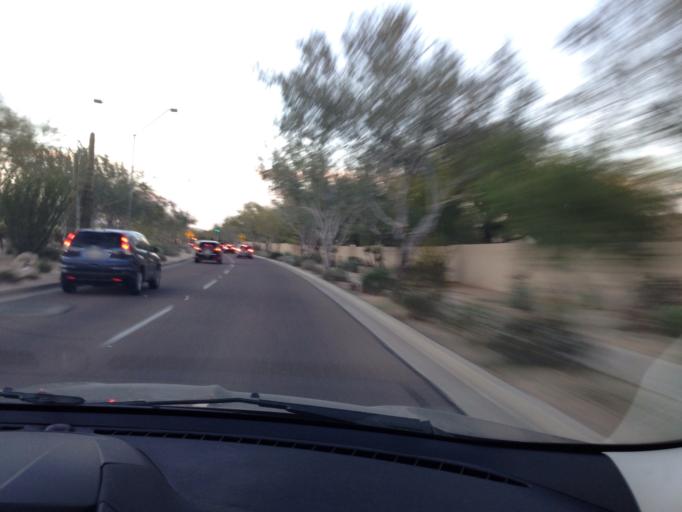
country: US
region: Arizona
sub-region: Maricopa County
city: Cave Creek
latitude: 33.7483
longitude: -111.9783
